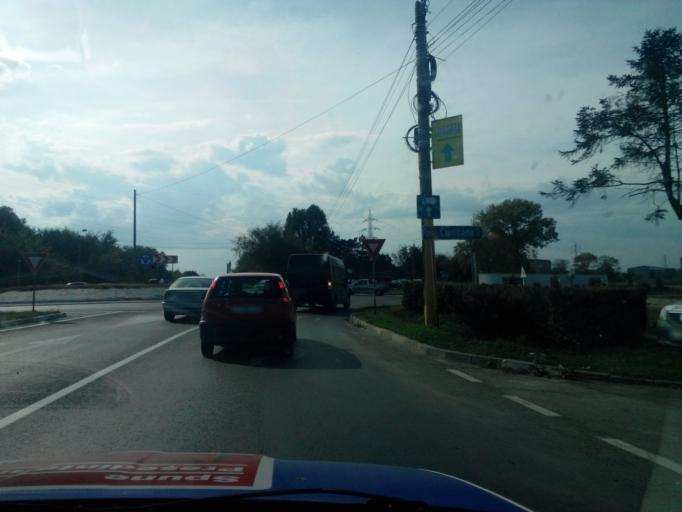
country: RO
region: Constanta
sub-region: Comuna Agigea
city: Agigea
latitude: 44.1322
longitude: 28.6178
